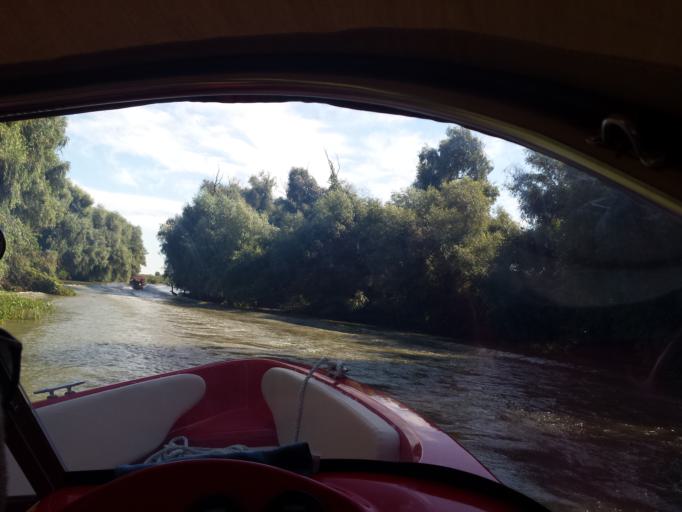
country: RO
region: Tulcea
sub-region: Comuna Pardina
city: Pardina
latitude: 45.2481
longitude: 29.0367
